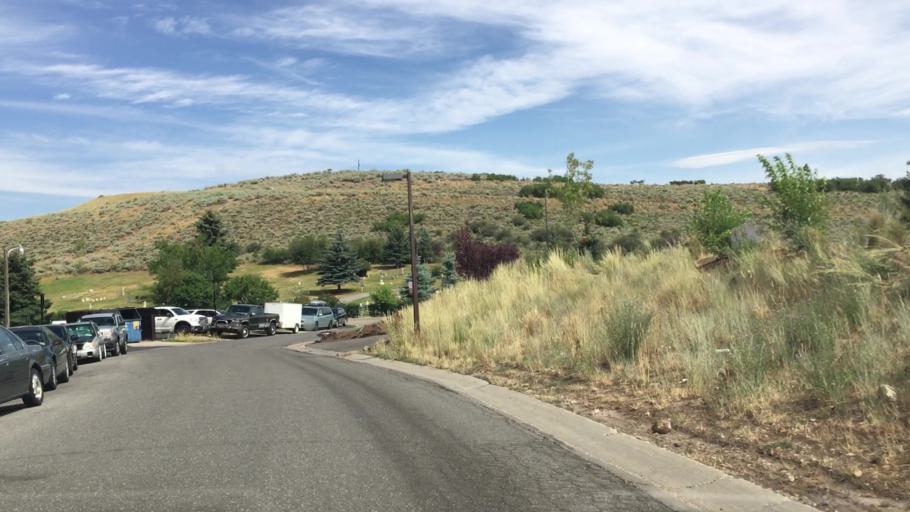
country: US
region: Utah
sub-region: Summit County
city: Park City
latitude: 40.6607
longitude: -111.5044
